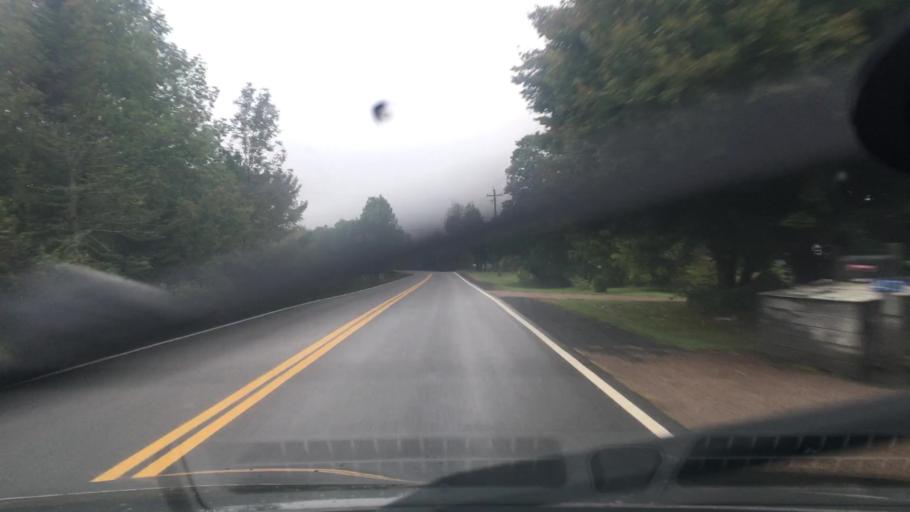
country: CA
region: Nova Scotia
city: Windsor
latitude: 44.9381
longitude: -64.1915
